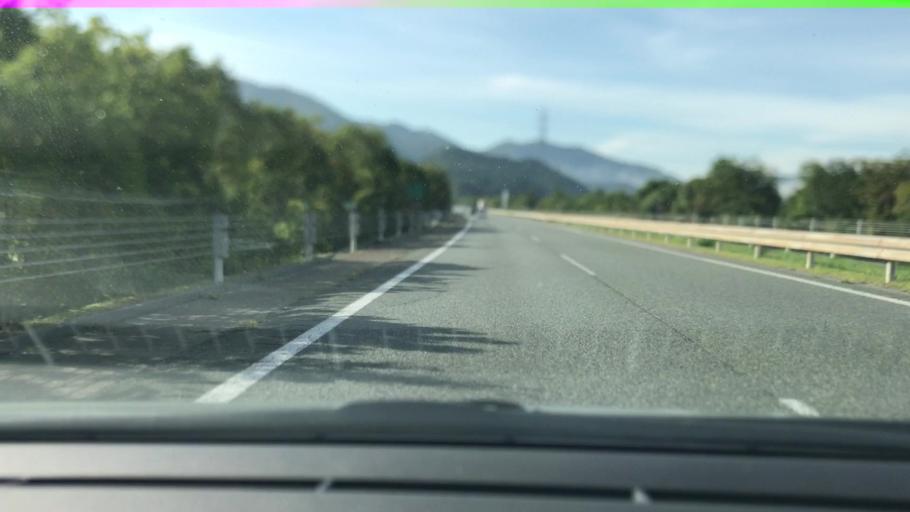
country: JP
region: Hyogo
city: Sasayama
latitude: 35.0496
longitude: 135.1829
